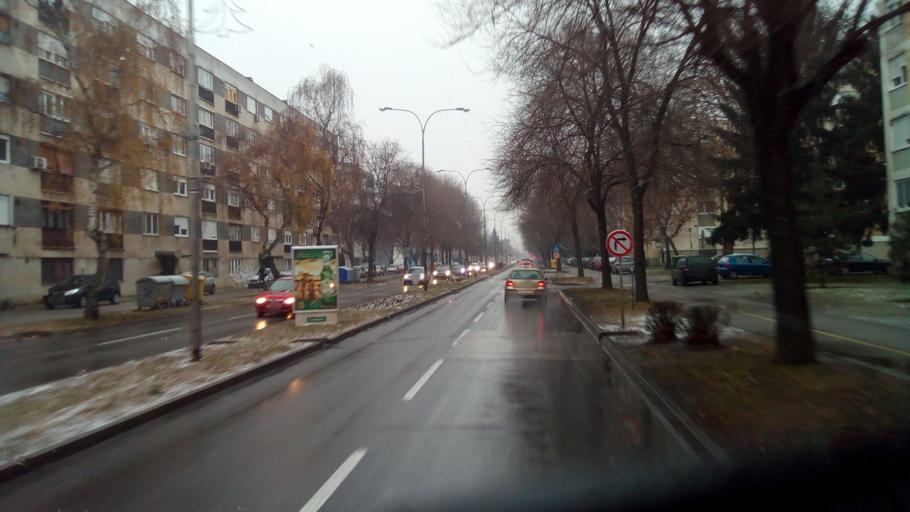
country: HR
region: Varazdinska
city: Varazdin
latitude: 46.2996
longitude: 16.3367
